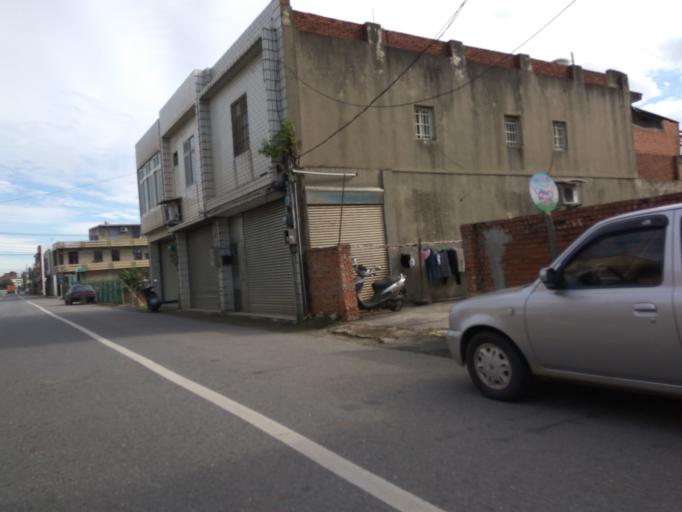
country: TW
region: Taiwan
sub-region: Hsinchu
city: Zhubei
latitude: 24.9637
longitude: 121.0962
